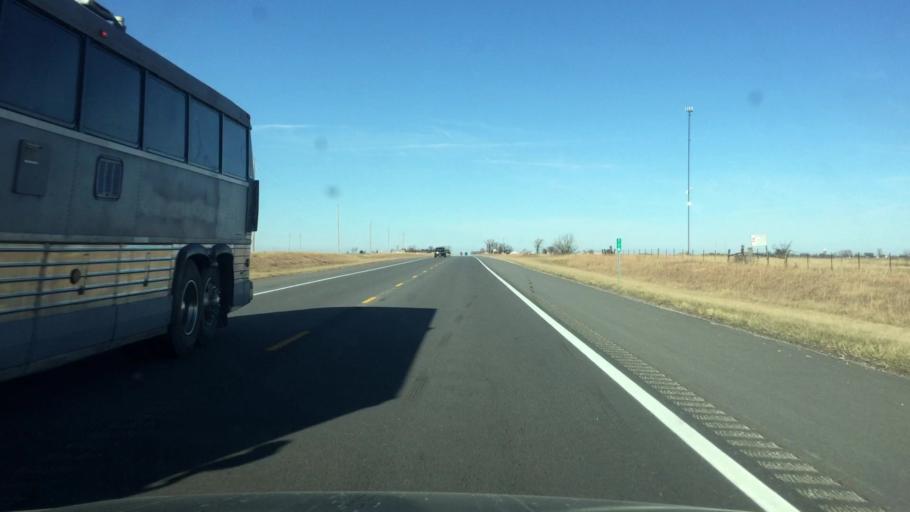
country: US
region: Kansas
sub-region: Anderson County
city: Garnett
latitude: 38.4153
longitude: -95.2487
